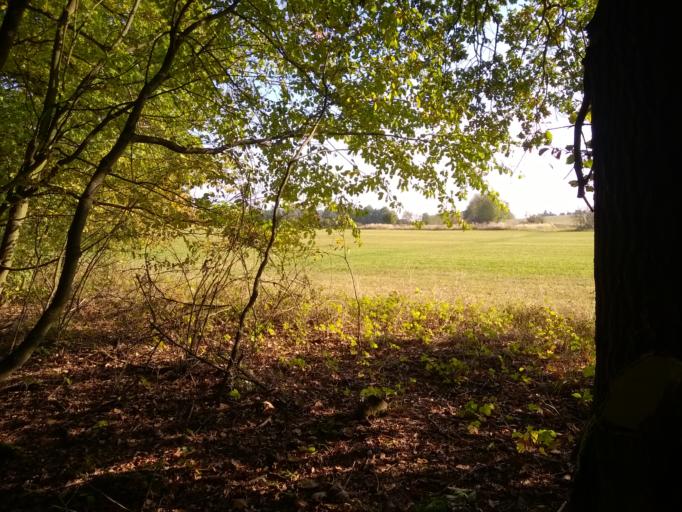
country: CZ
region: Central Bohemia
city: Kamenny Privoz
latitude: 49.8562
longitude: 14.4714
